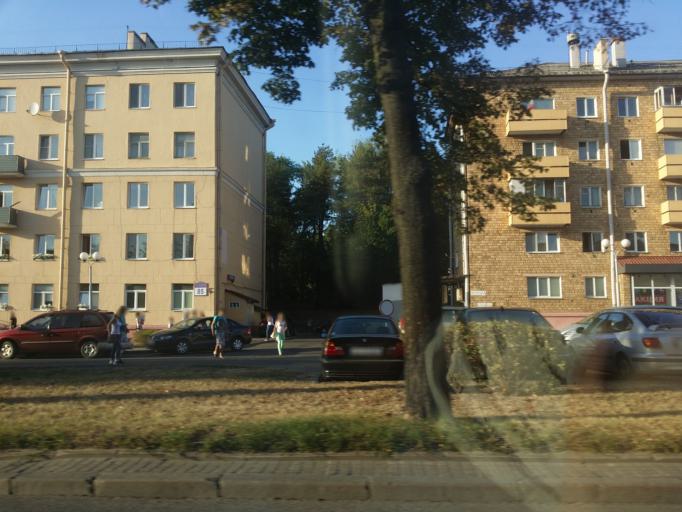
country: BY
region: Minsk
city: Minsk
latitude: 53.8743
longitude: 27.6322
